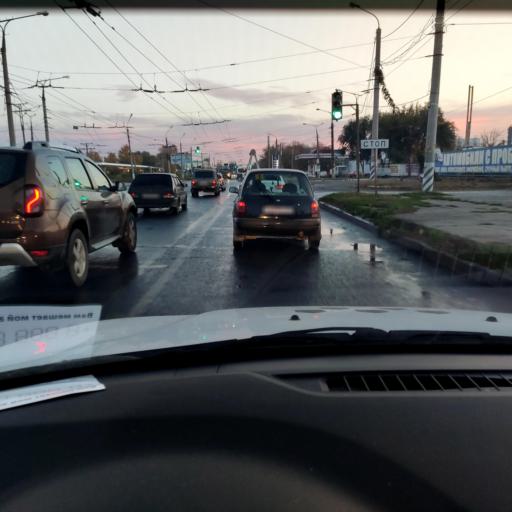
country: RU
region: Samara
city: Tol'yatti
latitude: 53.5322
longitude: 49.4389
